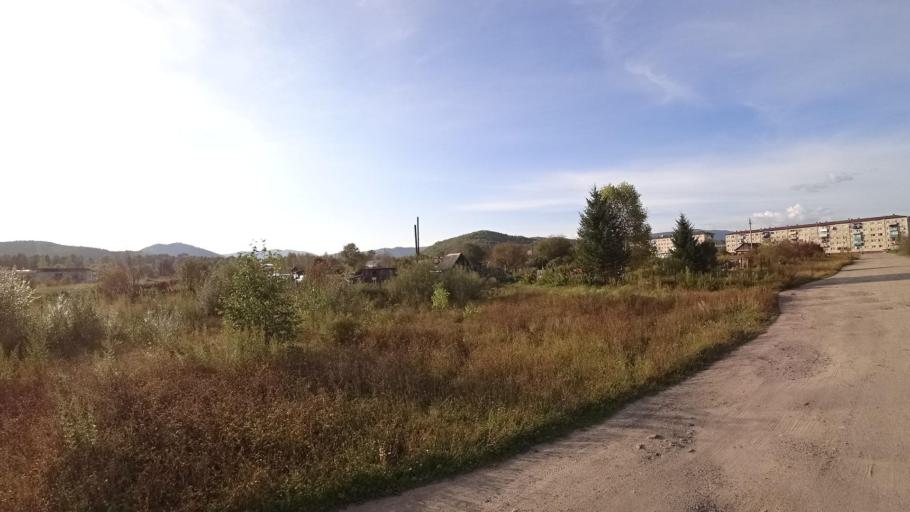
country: RU
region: Jewish Autonomous Oblast
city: Kul'dur
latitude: 49.1992
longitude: 131.6258
